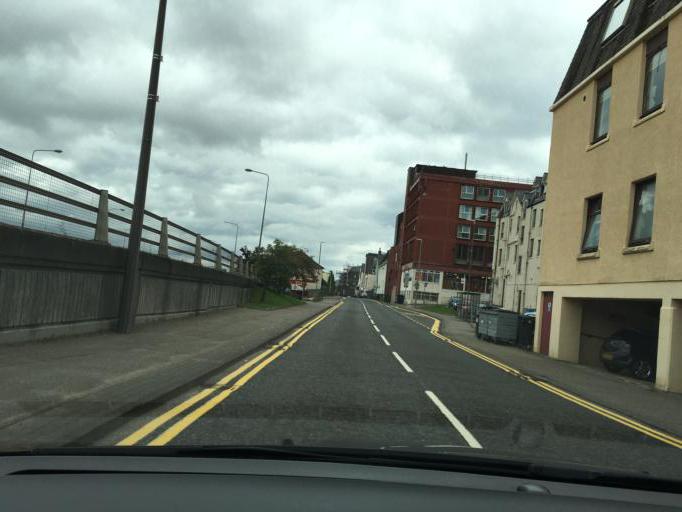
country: GB
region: Scotland
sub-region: Highland
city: Fort William
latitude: 56.8171
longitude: -5.1134
